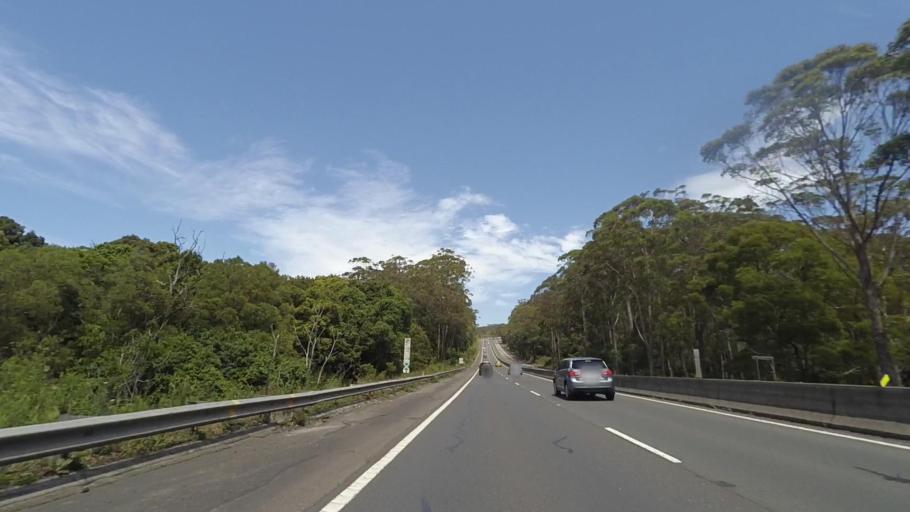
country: AU
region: New South Wales
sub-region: Wollongong
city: Corrimal
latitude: -34.3504
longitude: 150.8676
